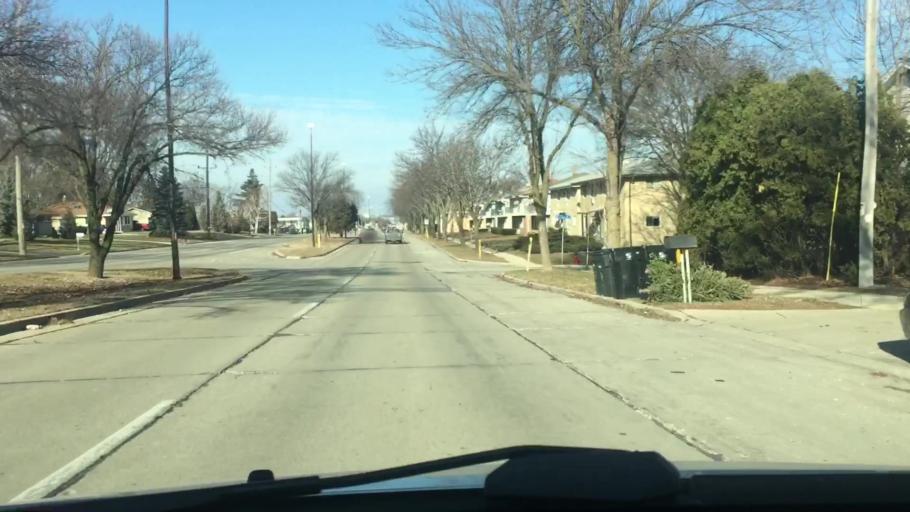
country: US
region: Wisconsin
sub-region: Waukesha County
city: Elm Grove
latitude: 43.0709
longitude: -88.0666
